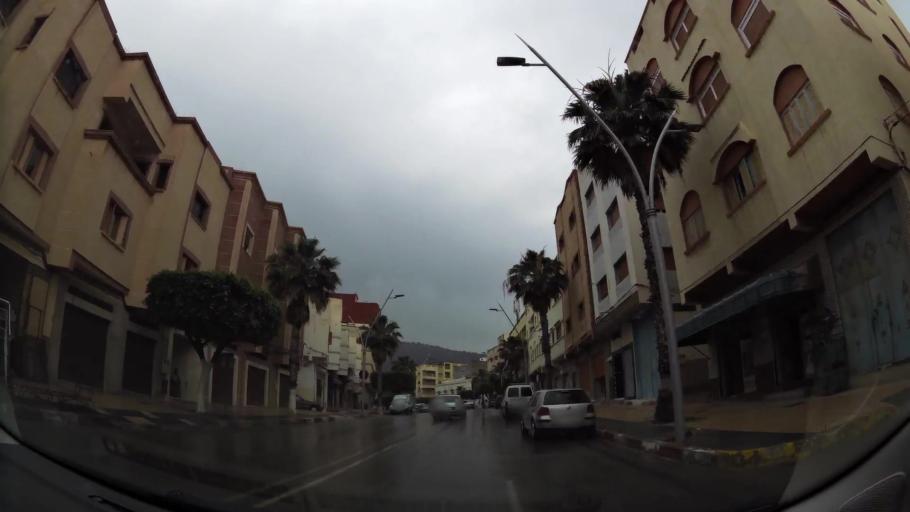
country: MA
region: Oriental
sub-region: Nador
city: Nador
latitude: 35.1547
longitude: -2.9977
